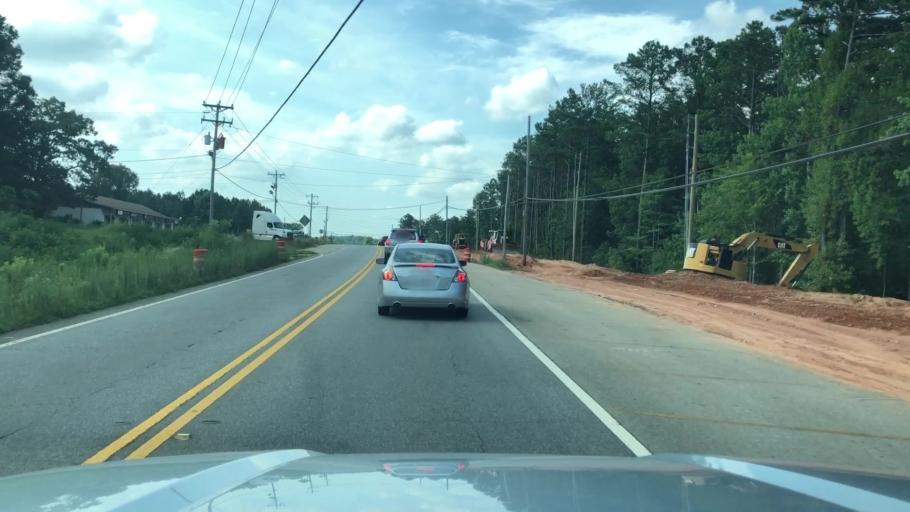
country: US
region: Georgia
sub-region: Douglas County
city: Douglasville
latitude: 33.7786
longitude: -84.7475
